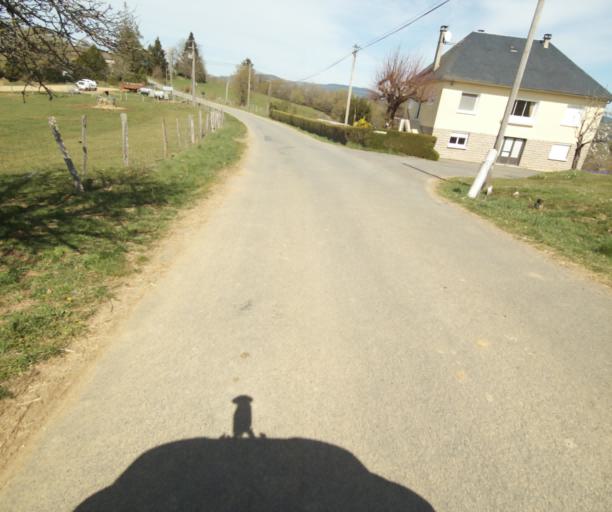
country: FR
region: Limousin
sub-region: Departement de la Correze
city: Seilhac
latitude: 45.3988
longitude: 1.7861
